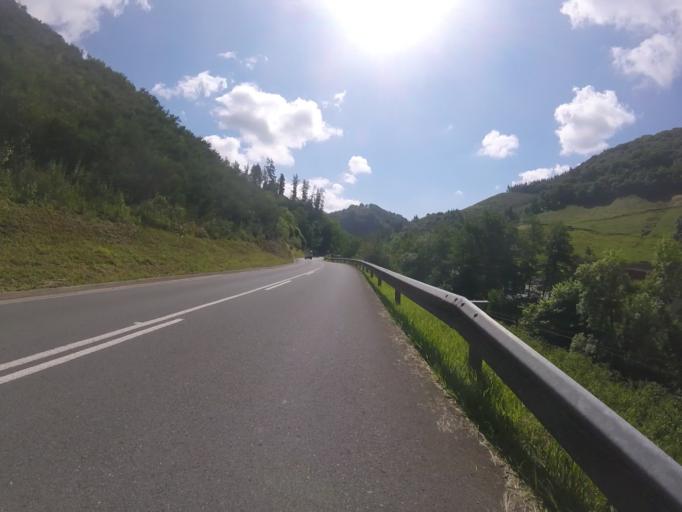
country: ES
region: Basque Country
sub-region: Provincia de Guipuzcoa
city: Azpeitia
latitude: 43.1802
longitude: -2.2337
